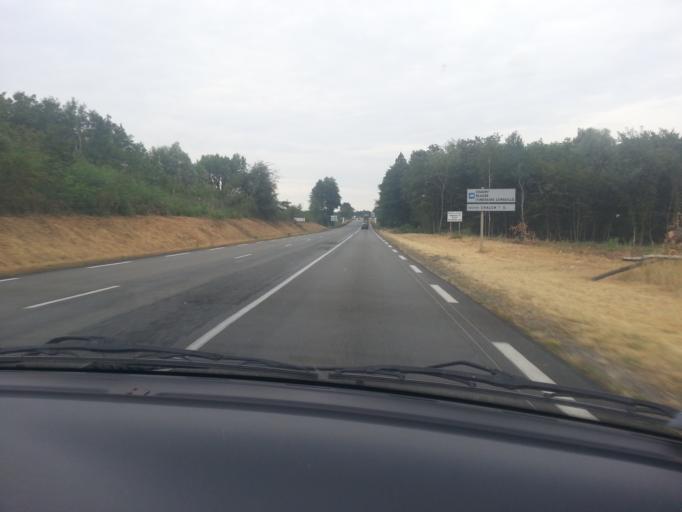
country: FR
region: Bourgogne
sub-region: Departement de Saone-et-Loire
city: Montchanin
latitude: 46.7442
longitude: 4.4882
